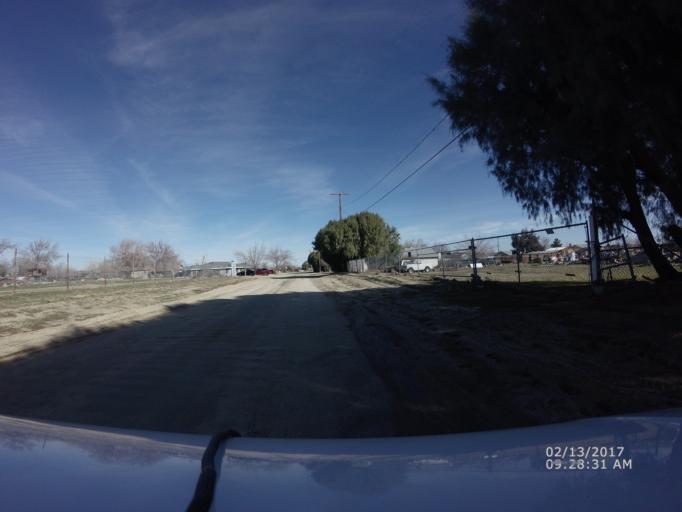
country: US
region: California
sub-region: Los Angeles County
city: Littlerock
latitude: 34.5417
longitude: -117.9625
